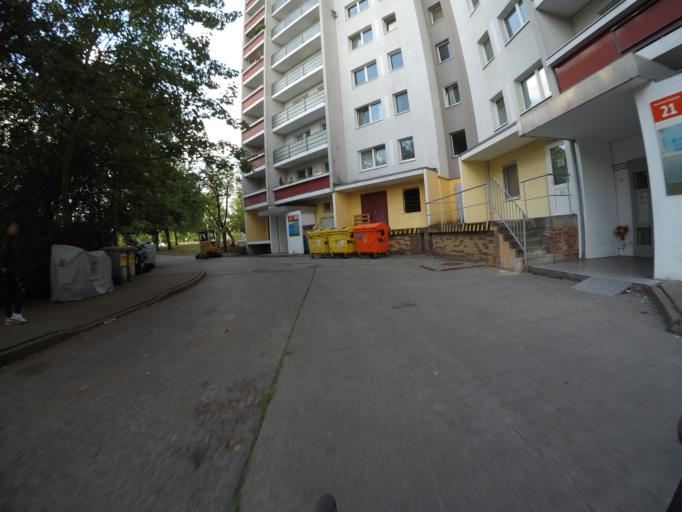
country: DE
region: Berlin
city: Marzahn
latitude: 52.5430
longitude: 13.5466
